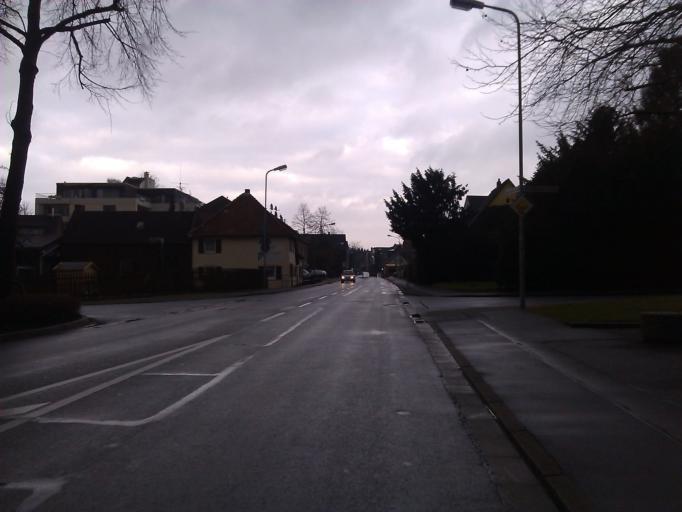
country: DE
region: North Rhine-Westphalia
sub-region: Regierungsbezirk Dusseldorf
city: Ratingen
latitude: 51.3286
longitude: 6.9057
